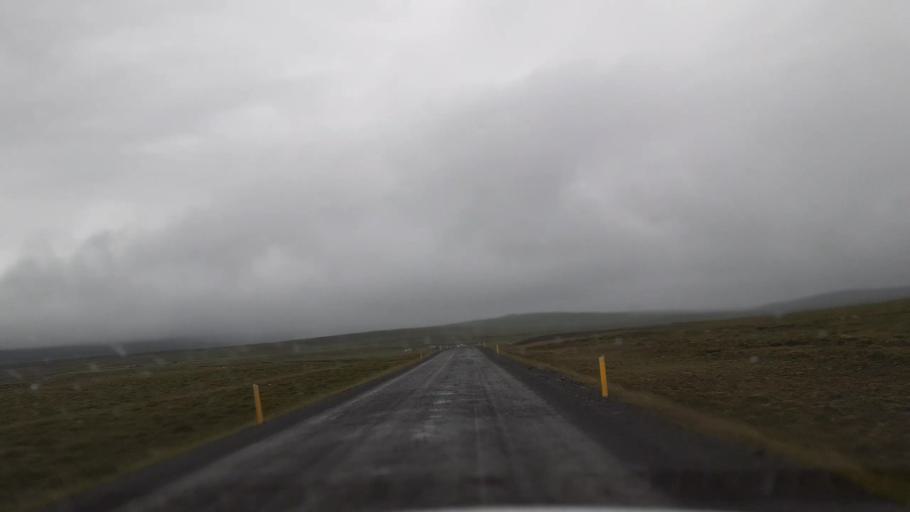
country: IS
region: East
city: Egilsstadir
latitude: 66.0489
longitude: -15.0932
